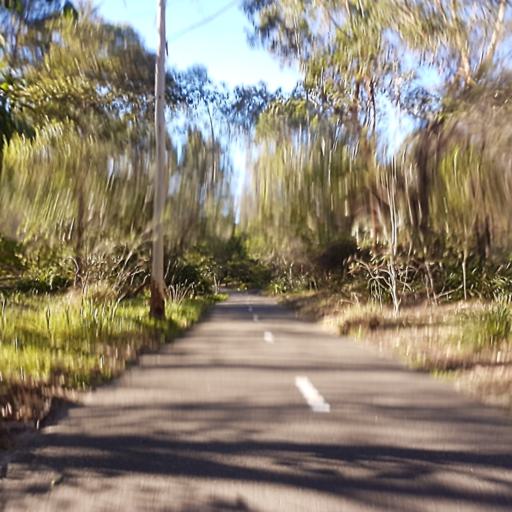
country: AU
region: New South Wales
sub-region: North Sydney
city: St Leonards
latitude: -33.8133
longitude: 151.2060
